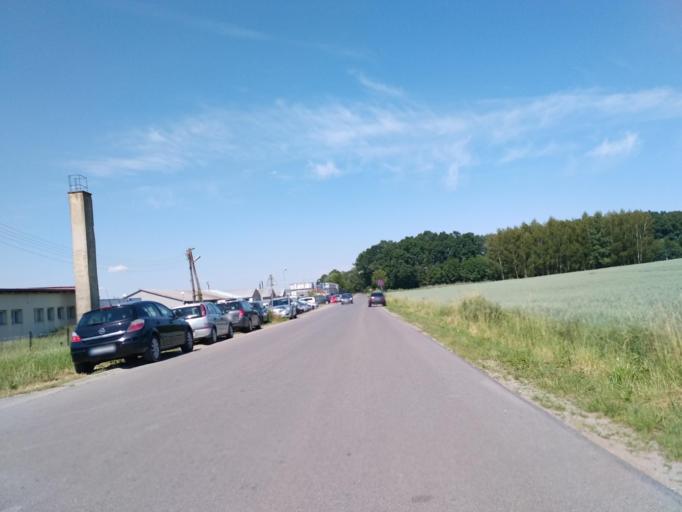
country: PL
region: Subcarpathian Voivodeship
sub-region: Powiat krosnienski
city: Korczyna
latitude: 49.7156
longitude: 21.7878
